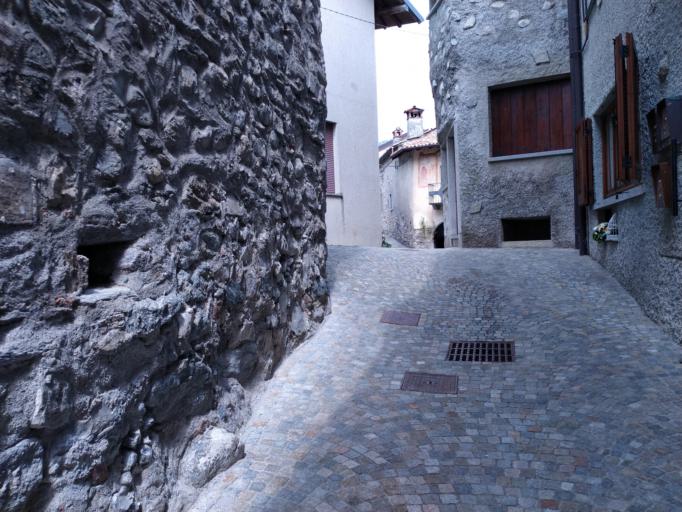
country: IT
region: Lombardy
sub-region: Provincia di Como
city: Rezzago
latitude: 45.8663
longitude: 9.2498
